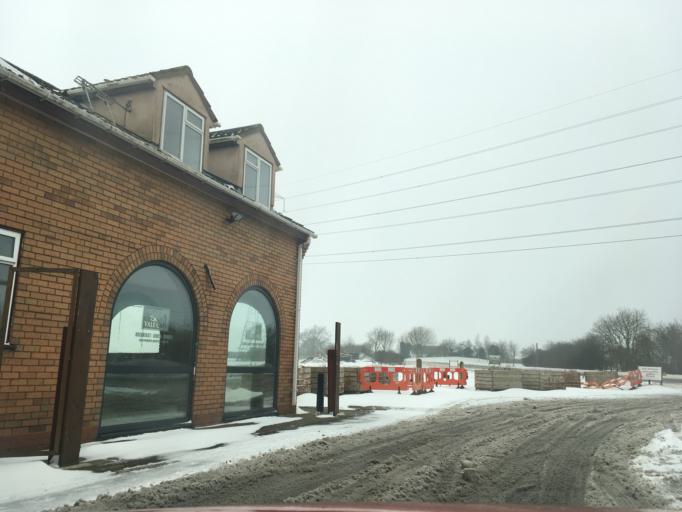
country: GB
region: England
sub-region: Worcestershire
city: Evesham
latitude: 52.0300
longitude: -1.9989
